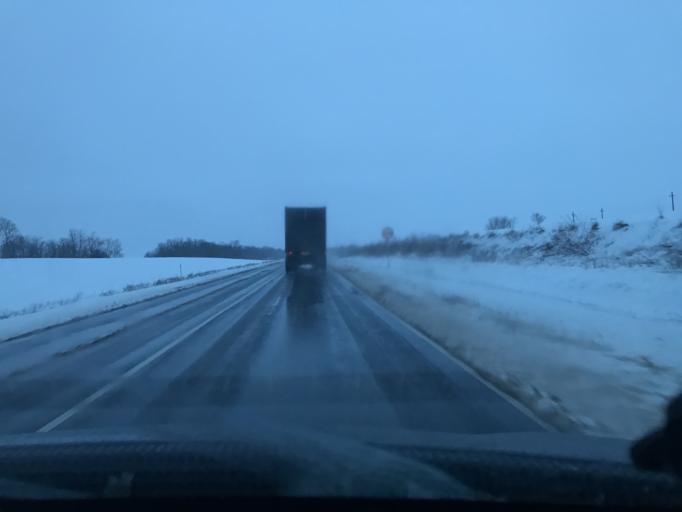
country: RU
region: Rostov
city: Letnik
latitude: 46.0264
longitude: 41.2111
